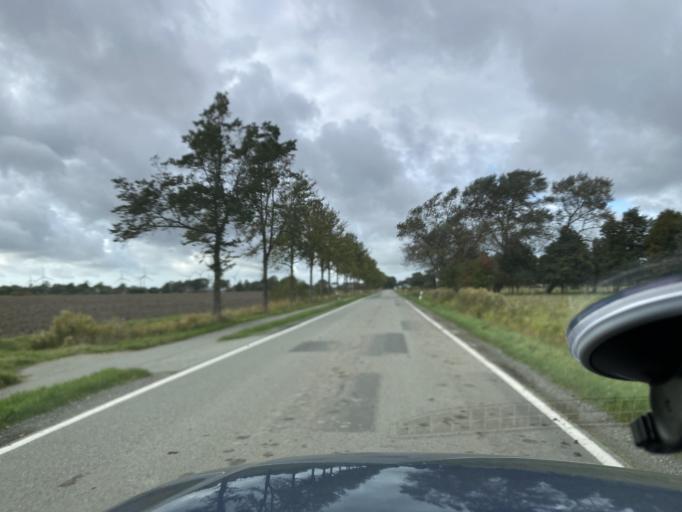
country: DE
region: Schleswig-Holstein
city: Neuenkirchen
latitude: 54.2340
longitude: 9.0086
